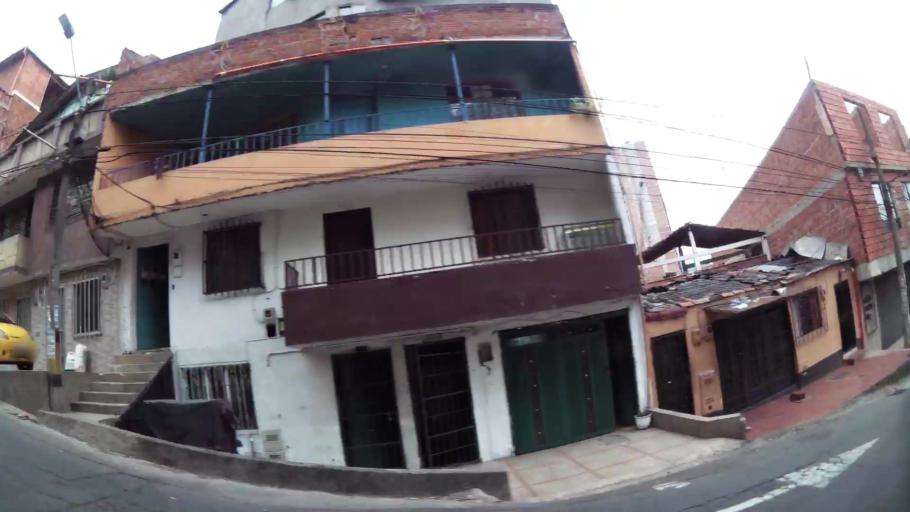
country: CO
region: Antioquia
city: Medellin
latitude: 6.2782
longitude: -75.5639
